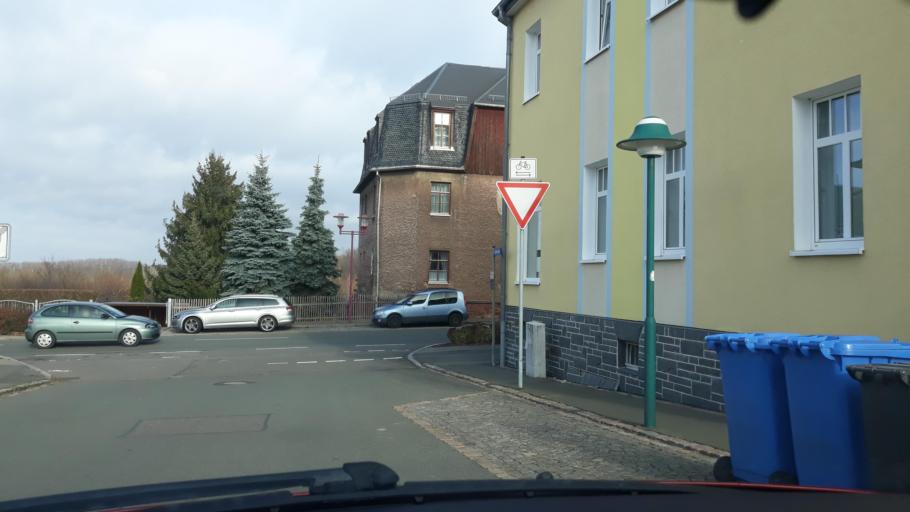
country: DE
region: Saxony
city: Wilkau-Hasslau
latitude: 50.6938
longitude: 12.5379
